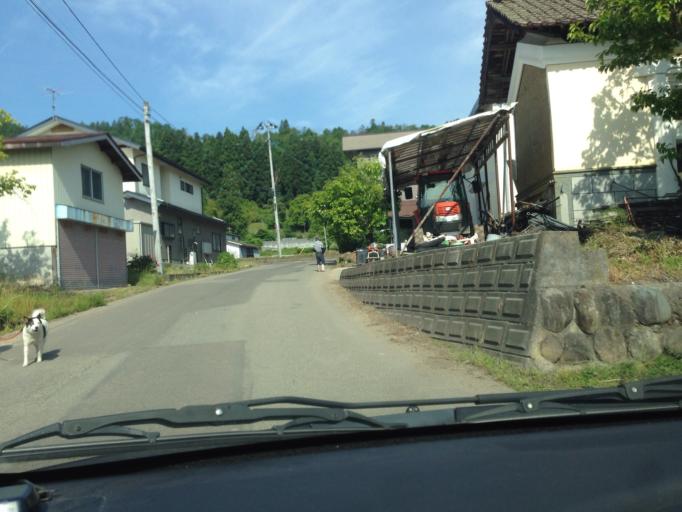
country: JP
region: Fukushima
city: Kitakata
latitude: 37.4865
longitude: 139.8167
